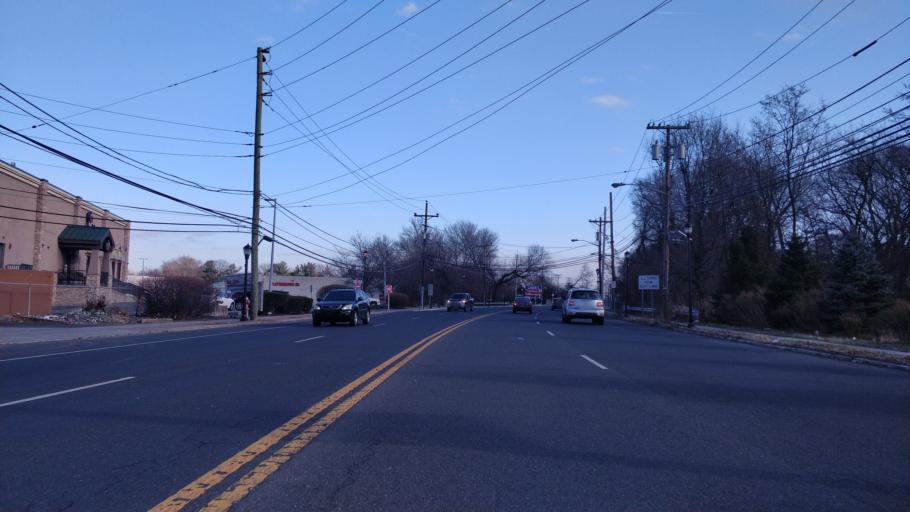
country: US
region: New Jersey
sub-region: Union County
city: Union
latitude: 40.6938
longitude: -74.2587
